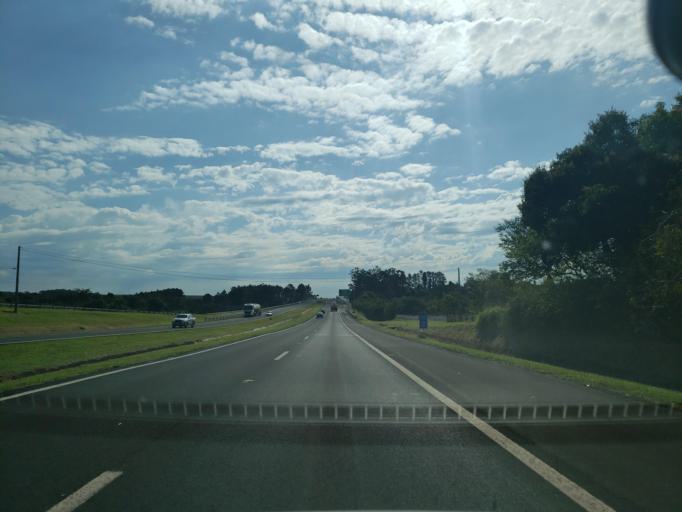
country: BR
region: Sao Paulo
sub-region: Pirajui
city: Pirajui
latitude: -21.9865
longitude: -49.4432
